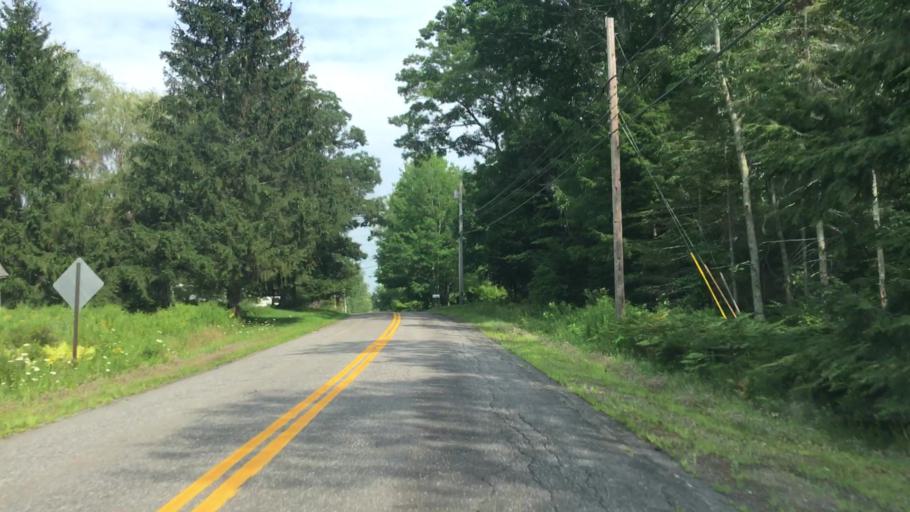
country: US
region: Maine
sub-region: Lincoln County
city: Waldoboro
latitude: 44.0978
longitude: -69.4062
